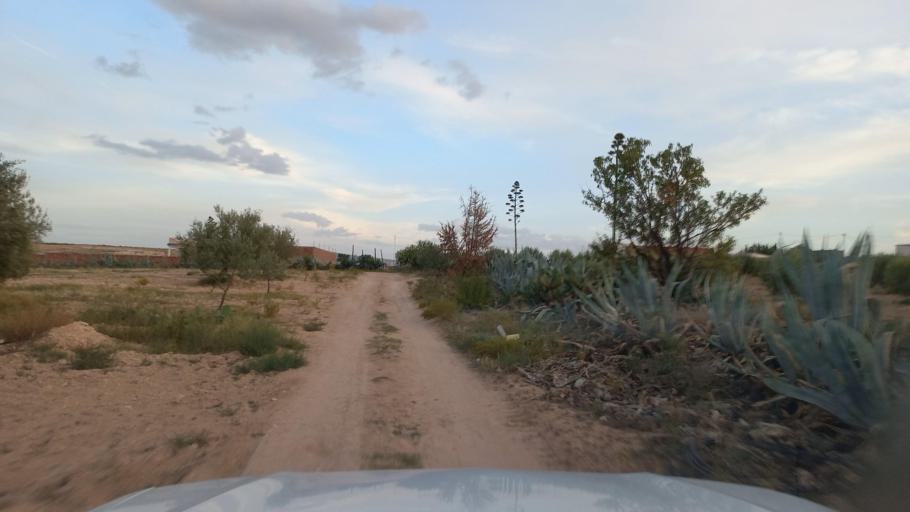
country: TN
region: Al Qasrayn
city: Sbiba
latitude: 35.4106
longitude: 9.1043
